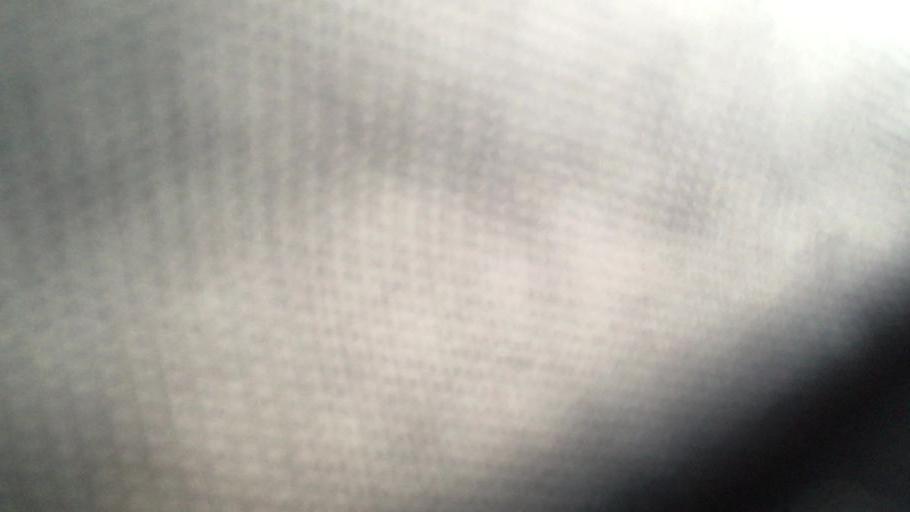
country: US
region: Maryland
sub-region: Somerset County
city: Princess Anne
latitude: 38.1673
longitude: -75.6891
